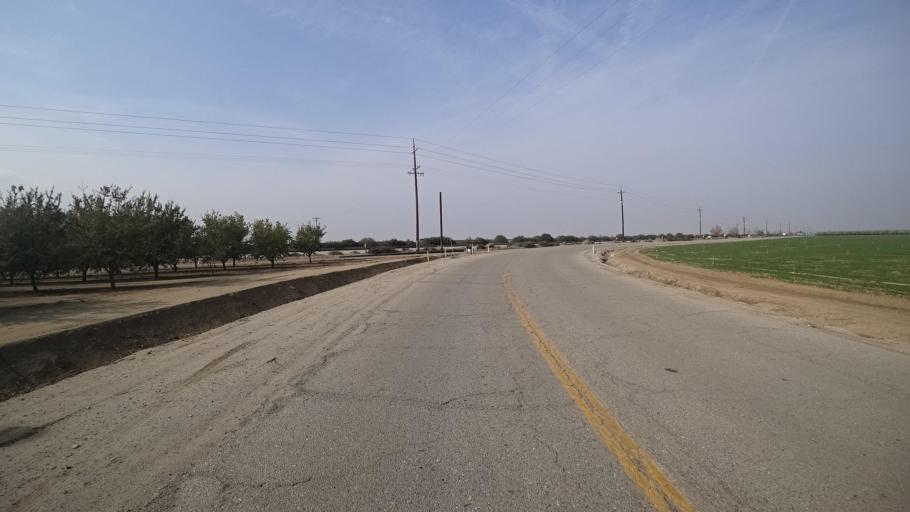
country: US
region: California
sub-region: Kern County
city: Weedpatch
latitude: 35.0341
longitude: -118.9594
